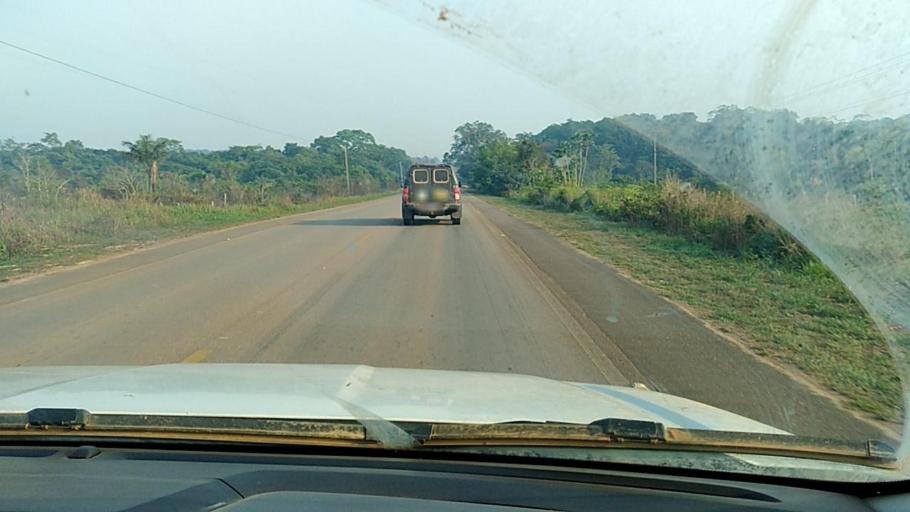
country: BR
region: Rondonia
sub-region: Porto Velho
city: Porto Velho
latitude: -8.7169
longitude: -63.9830
